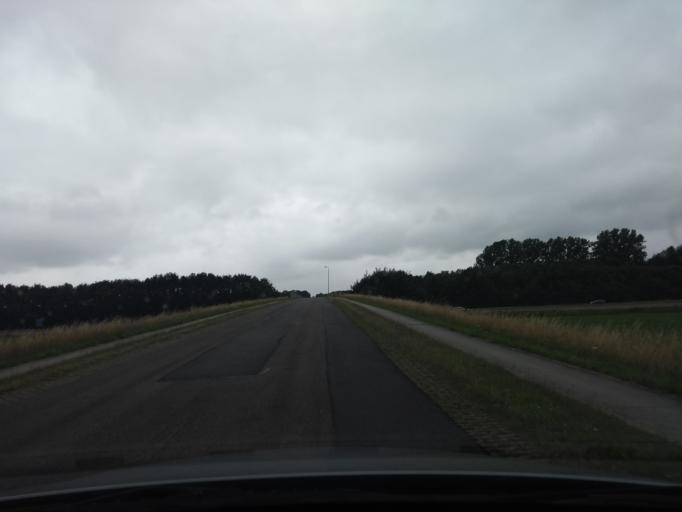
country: NL
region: Overijssel
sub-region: Gemeente Staphorst
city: Staphorst
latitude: 52.6786
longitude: 6.2994
